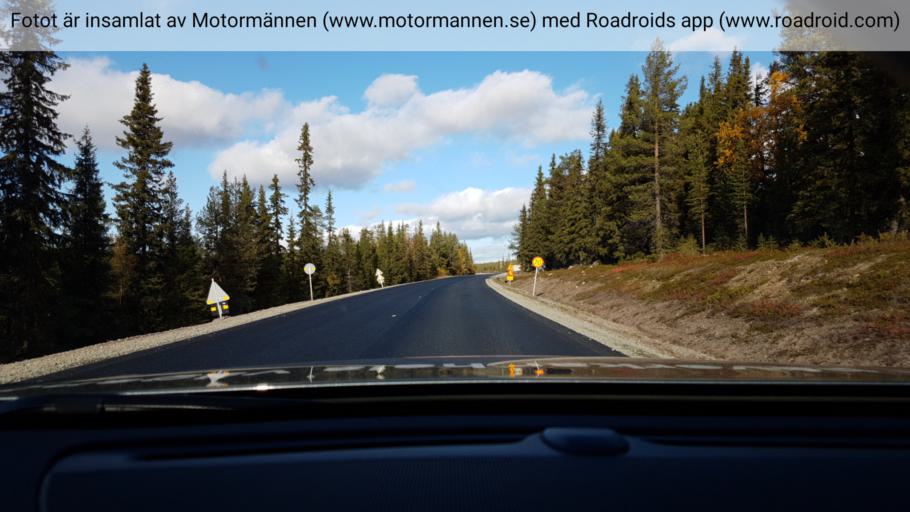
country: SE
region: Norrbotten
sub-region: Arjeplogs Kommun
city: Arjeplog
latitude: 65.9211
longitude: 18.3163
